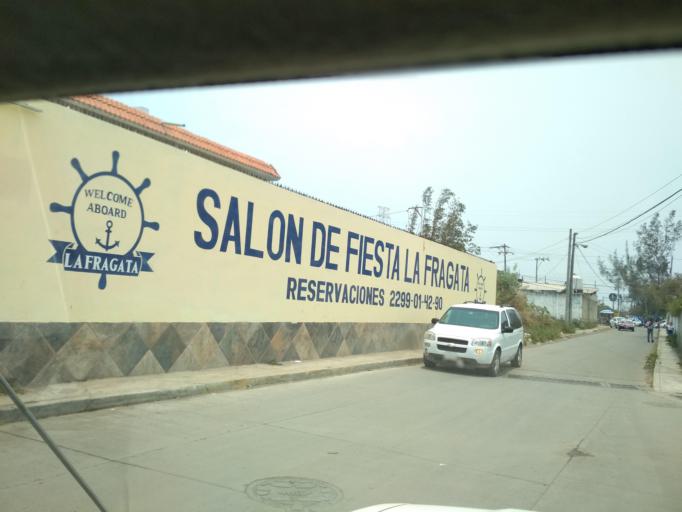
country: MX
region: Veracruz
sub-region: Veracruz
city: Las Amapolas
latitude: 19.1610
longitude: -96.2092
